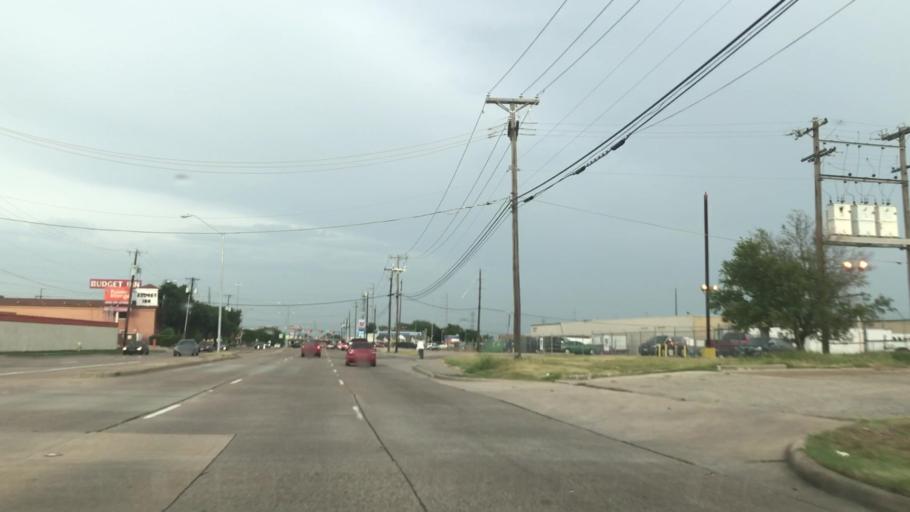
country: US
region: Texas
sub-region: Dallas County
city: Garland
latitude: 32.8640
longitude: -96.6688
